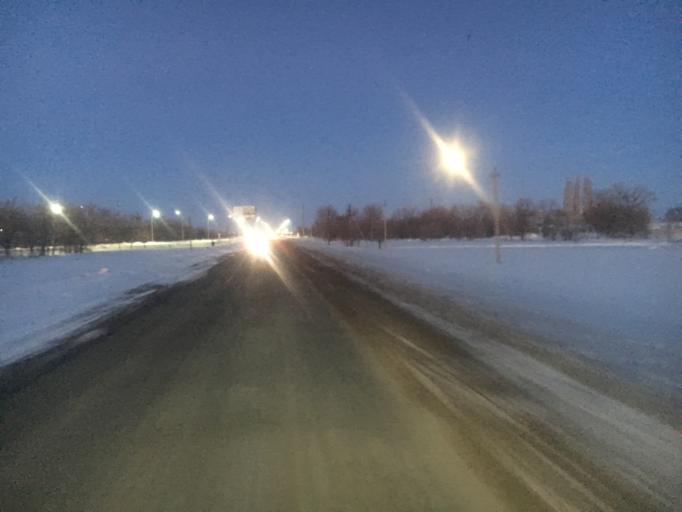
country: KZ
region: Batys Qazaqstan
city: Oral
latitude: 51.1553
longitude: 51.4928
